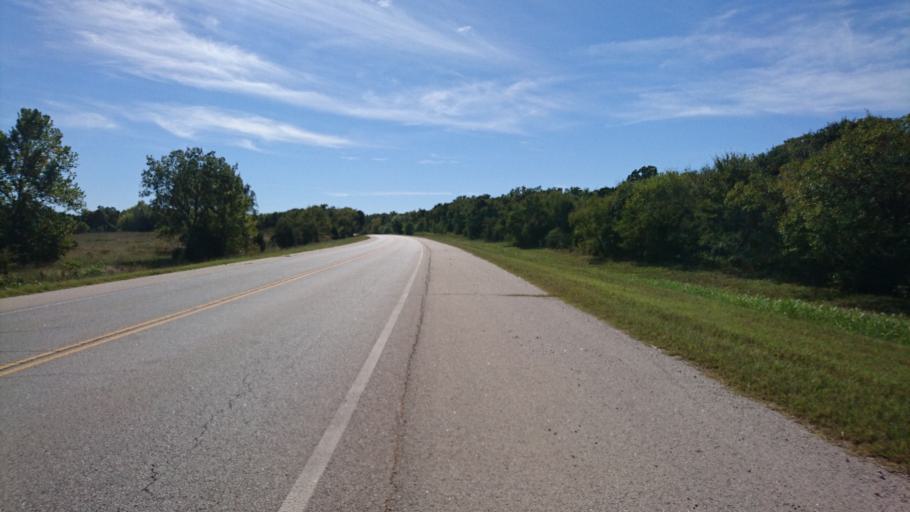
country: US
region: Oklahoma
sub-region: Lincoln County
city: Stroud
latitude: 35.7362
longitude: -96.7199
